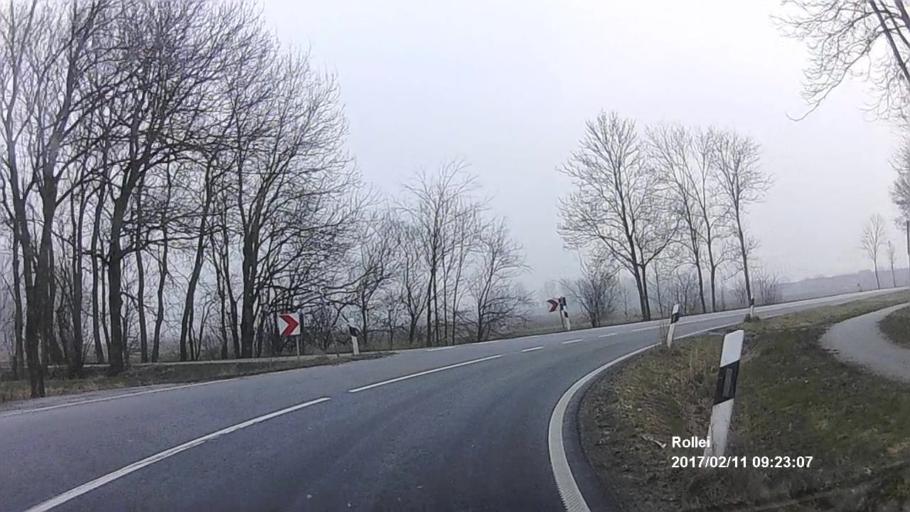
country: DE
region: Lower Saxony
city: Wirdum
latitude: 53.4799
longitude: 7.1375
